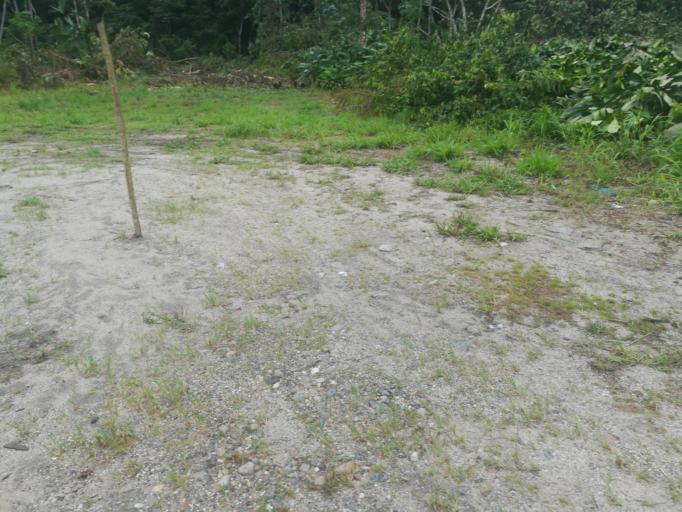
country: EC
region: Napo
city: Tena
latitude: -1.0488
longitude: -77.7990
